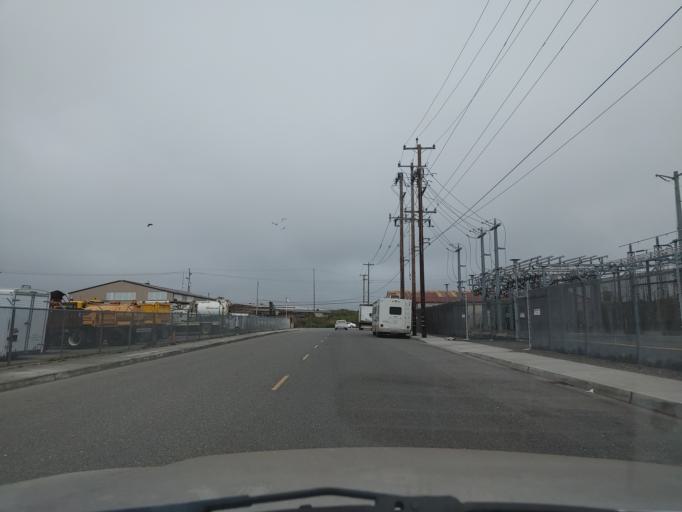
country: US
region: California
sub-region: Humboldt County
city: Eureka
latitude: 40.7930
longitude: -124.1806
